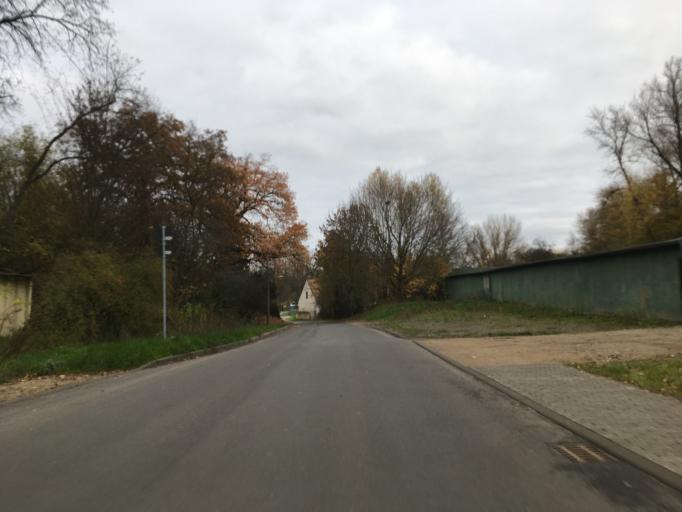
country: DE
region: Brandenburg
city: Frankfurt (Oder)
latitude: 52.3151
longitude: 14.5511
